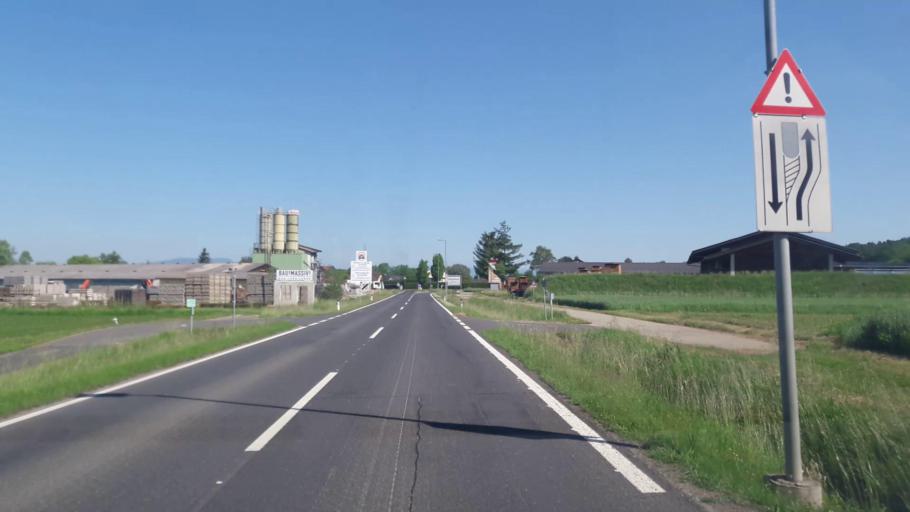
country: AT
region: Styria
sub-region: Politischer Bezirk Hartberg-Fuerstenfeld
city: Burgau
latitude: 47.1489
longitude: 16.1170
